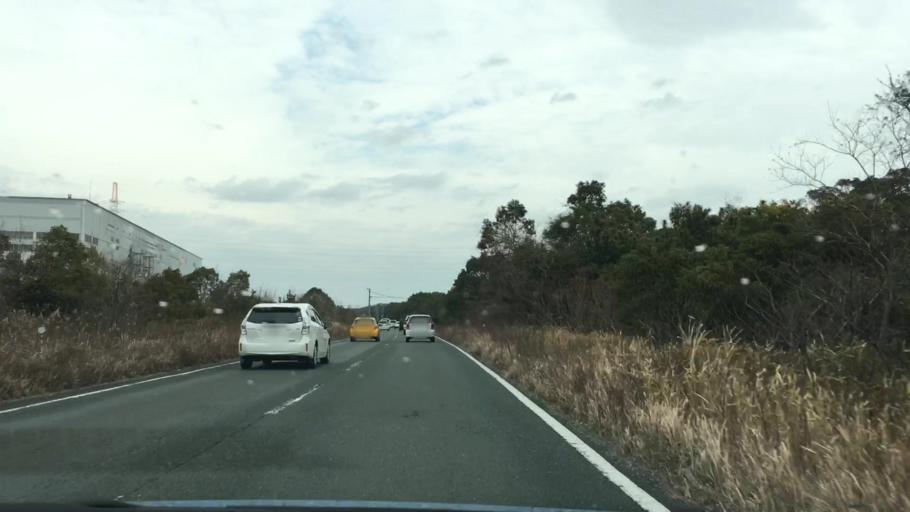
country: JP
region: Aichi
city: Toyohashi
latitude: 34.7097
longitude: 137.3344
